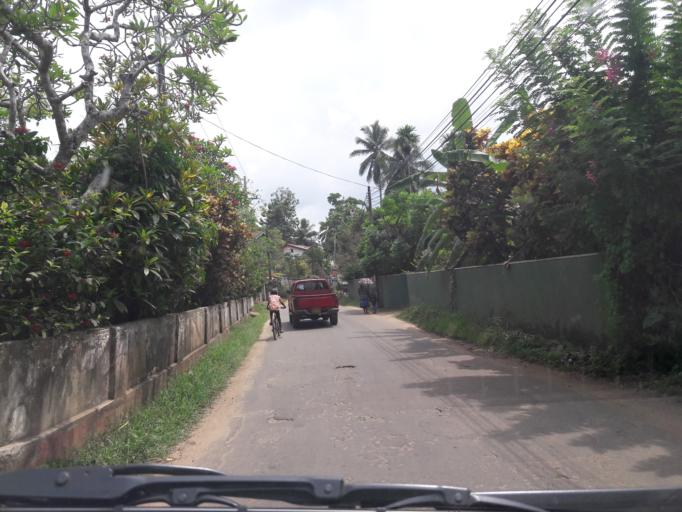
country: LK
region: Southern
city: Hikkaduwa
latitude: 6.0956
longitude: 80.1508
